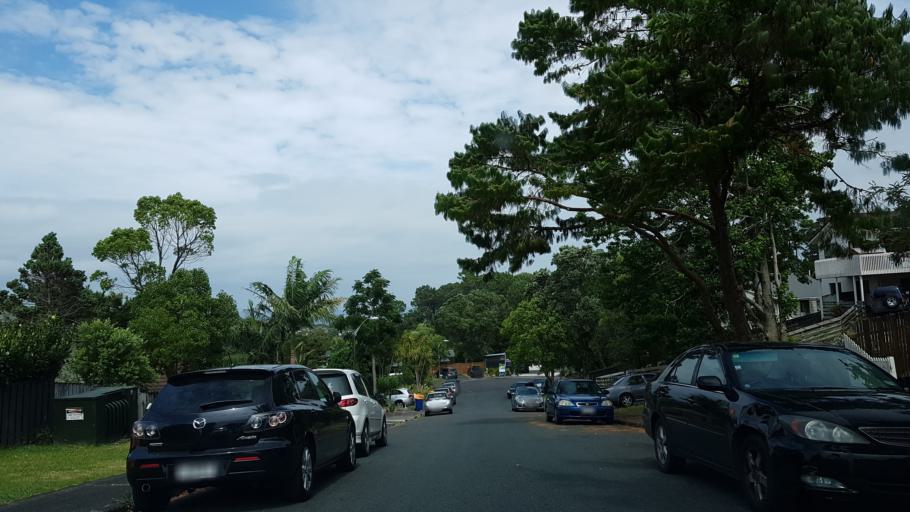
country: NZ
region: Auckland
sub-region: Auckland
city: North Shore
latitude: -36.7682
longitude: 174.7171
